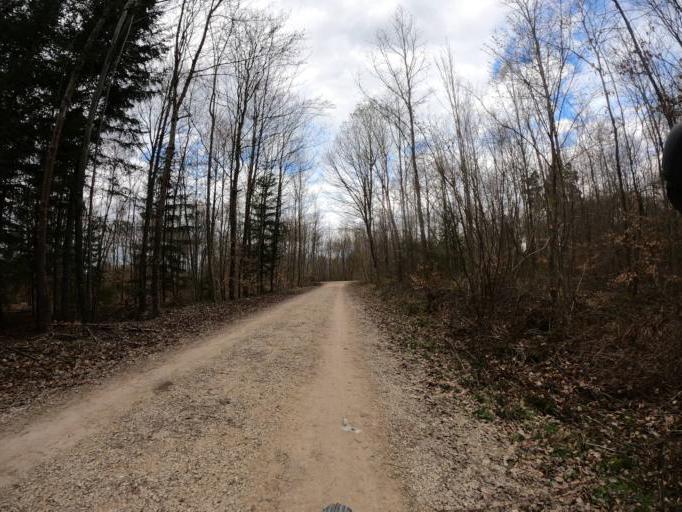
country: DE
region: Baden-Wuerttemberg
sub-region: Tuebingen Region
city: Gomaringen
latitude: 48.4601
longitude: 9.1294
